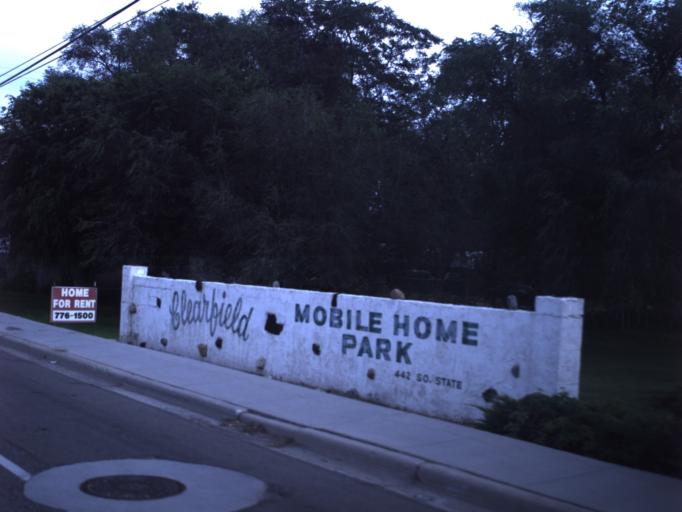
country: US
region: Utah
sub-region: Davis County
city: Clearfield
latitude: 41.1078
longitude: -112.0203
